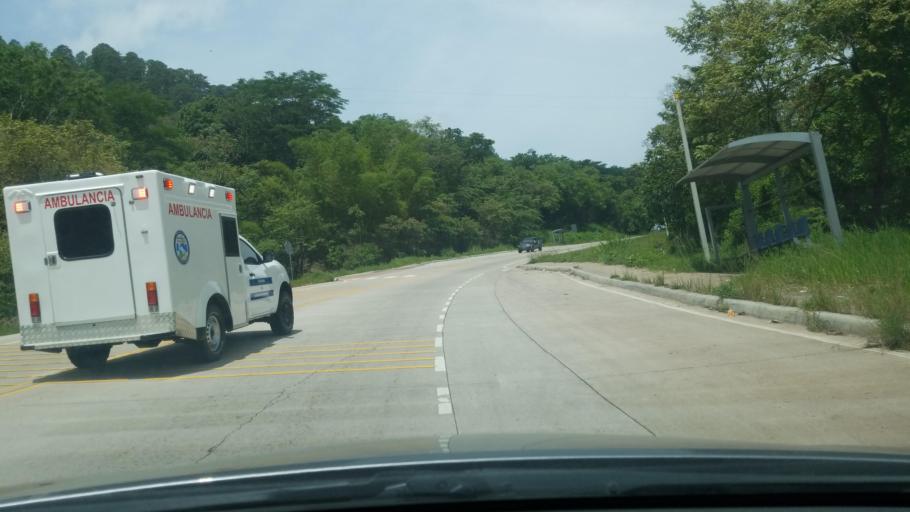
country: HN
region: Copan
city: Agua Caliente
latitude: 14.8738
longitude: -88.7777
